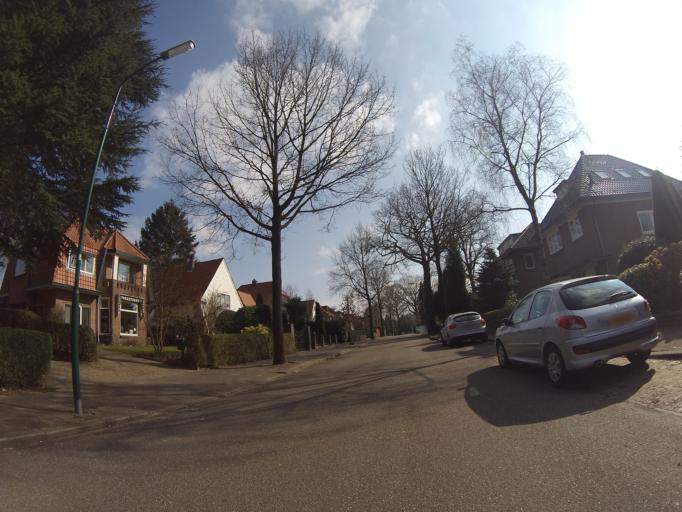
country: NL
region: Utrecht
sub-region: Gemeente Soest
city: Soest
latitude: 52.1833
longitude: 5.2891
